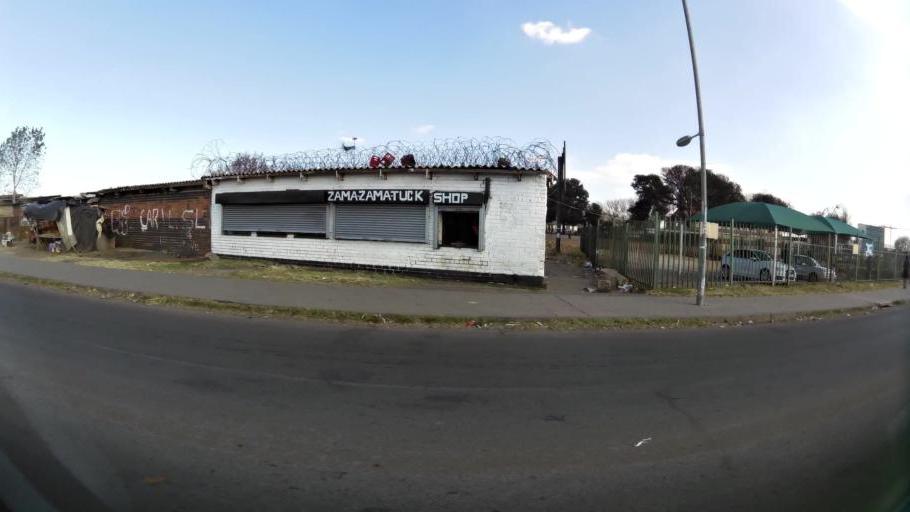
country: ZA
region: Gauteng
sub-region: City of Johannesburg Metropolitan Municipality
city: Soweto
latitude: -26.2532
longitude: 27.8998
